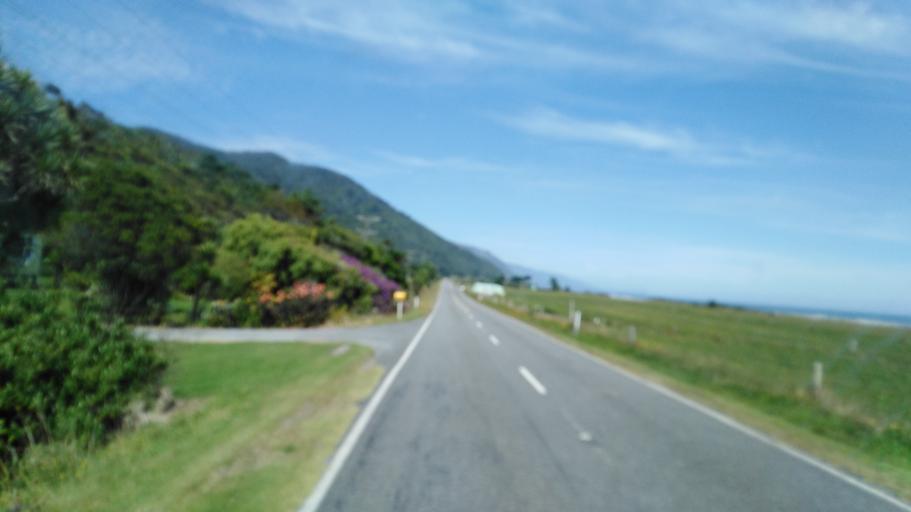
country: NZ
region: West Coast
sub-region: Buller District
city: Westport
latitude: -41.5500
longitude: 171.9228
